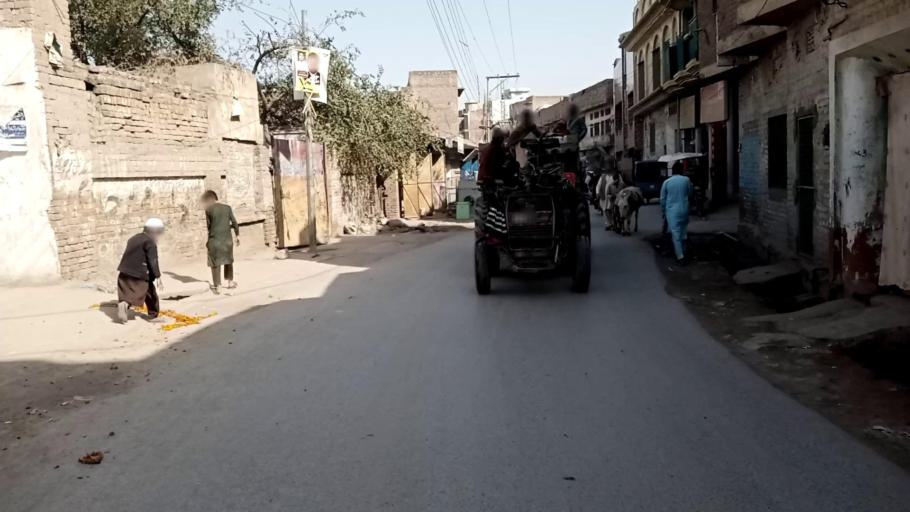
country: PK
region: Khyber Pakhtunkhwa
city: Peshawar
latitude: 33.9973
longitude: 71.5782
